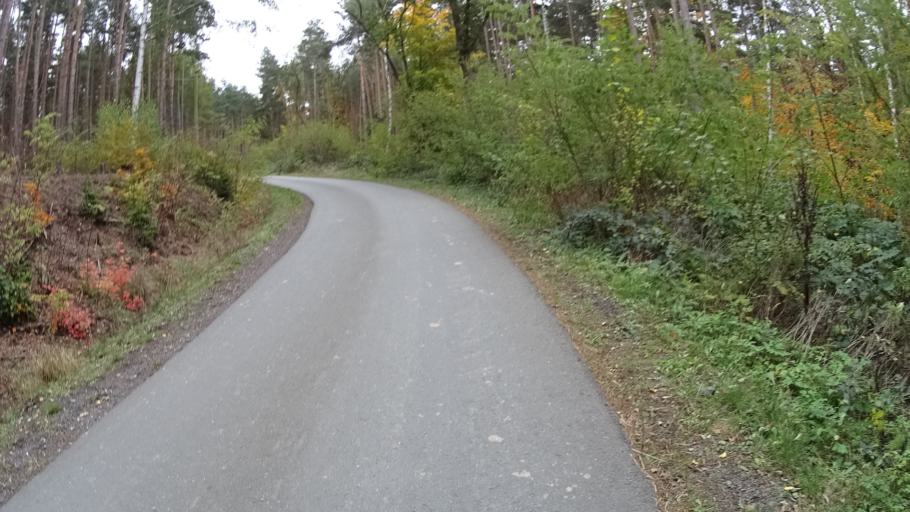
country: DE
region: Thuringia
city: Freienorla
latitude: 50.7667
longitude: 11.5531
